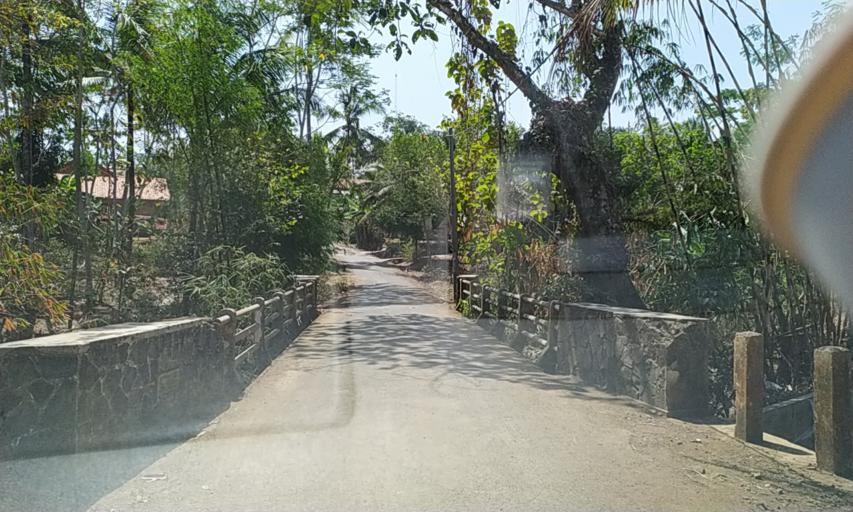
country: ID
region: Central Java
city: Prapagan
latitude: -7.5911
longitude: 108.9879
